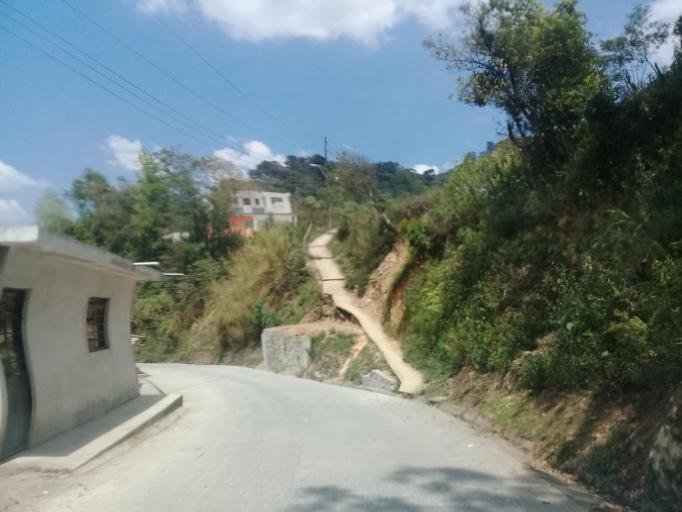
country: MX
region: Veracruz
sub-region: Tlilapan
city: Tonalixco
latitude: 18.7952
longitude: -97.0558
